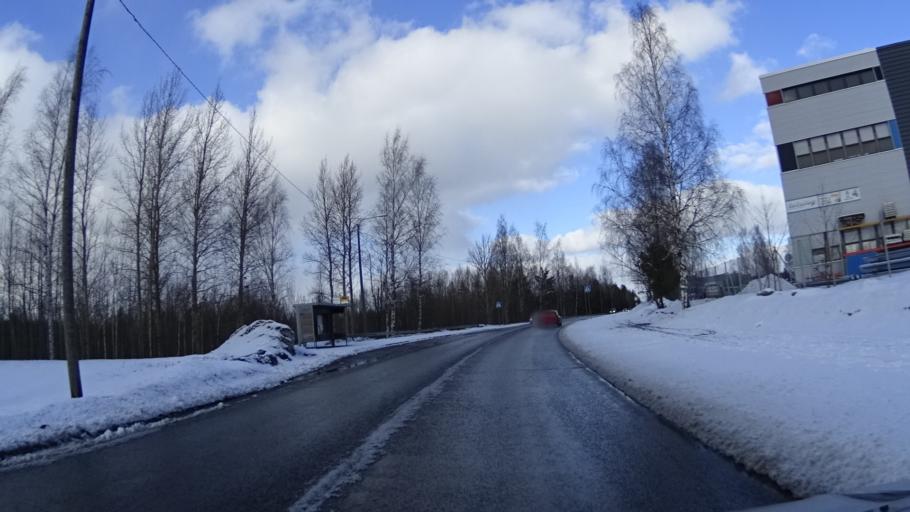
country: FI
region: Uusimaa
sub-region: Helsinki
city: Vantaa
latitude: 60.2989
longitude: 25.0864
